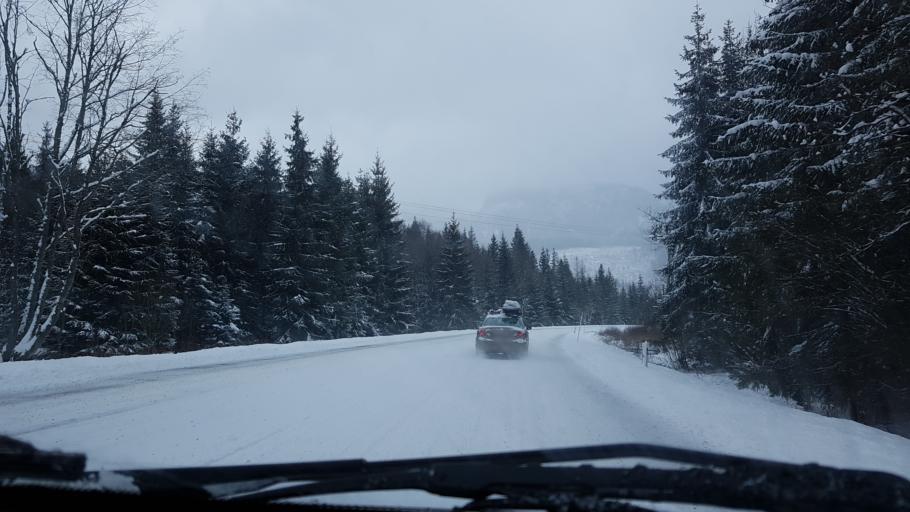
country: PL
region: Lesser Poland Voivodeship
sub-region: Powiat tatrzanski
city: Bukowina Tatrzanska
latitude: 49.2878
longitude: 20.1748
